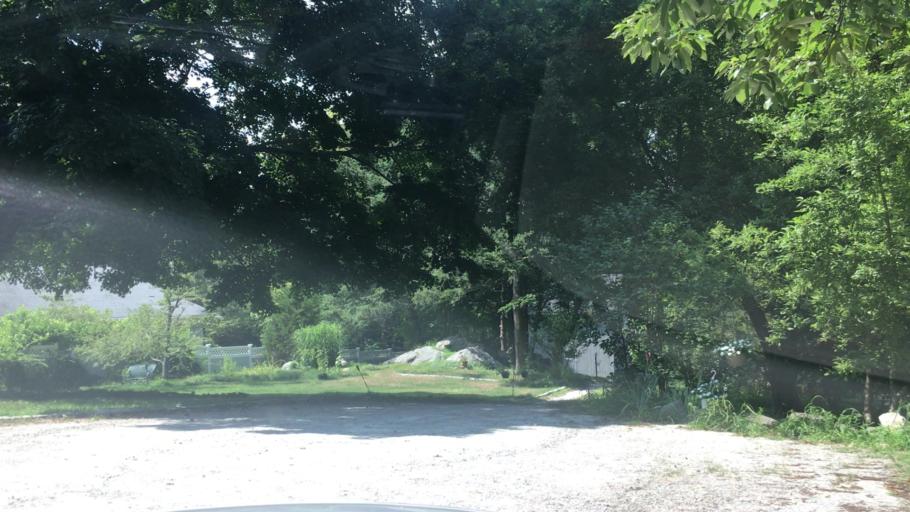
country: US
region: Connecticut
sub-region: Middlesex County
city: Essex Village
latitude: 41.3590
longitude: -72.4018
